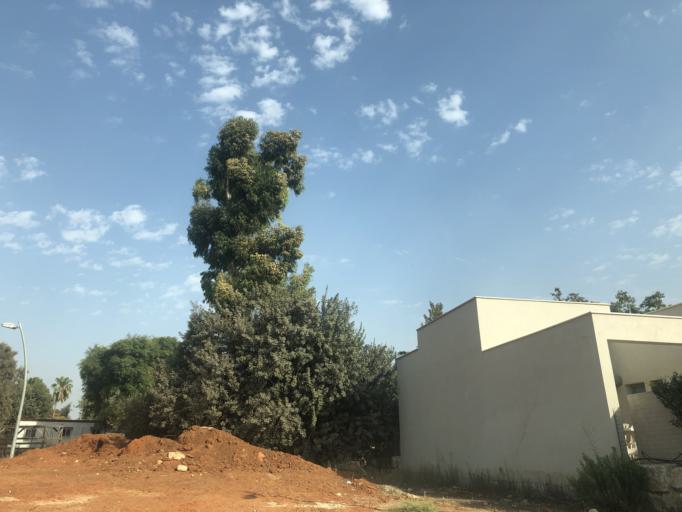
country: IL
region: Central District
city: Rosh Ha'Ayin
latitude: 32.0839
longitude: 34.9349
